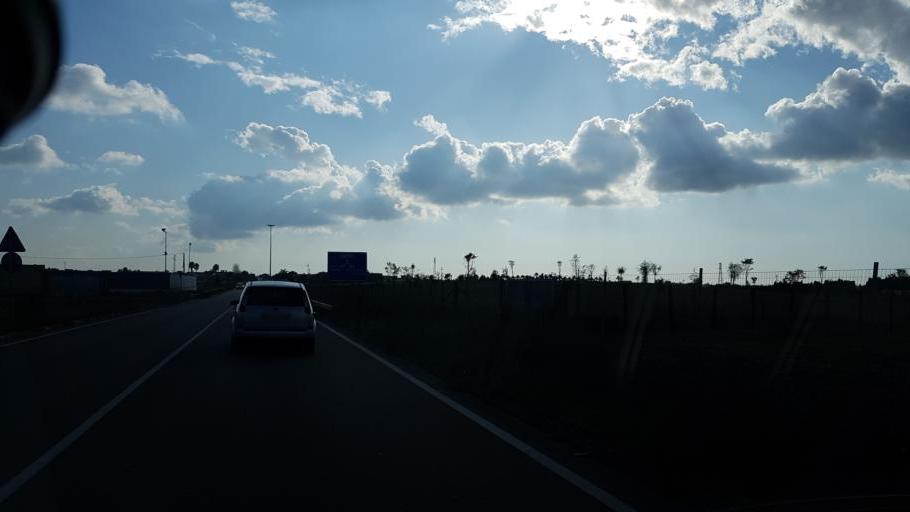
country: IT
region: Apulia
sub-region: Provincia di Lecce
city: Veglie
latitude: 40.3521
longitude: 17.9685
